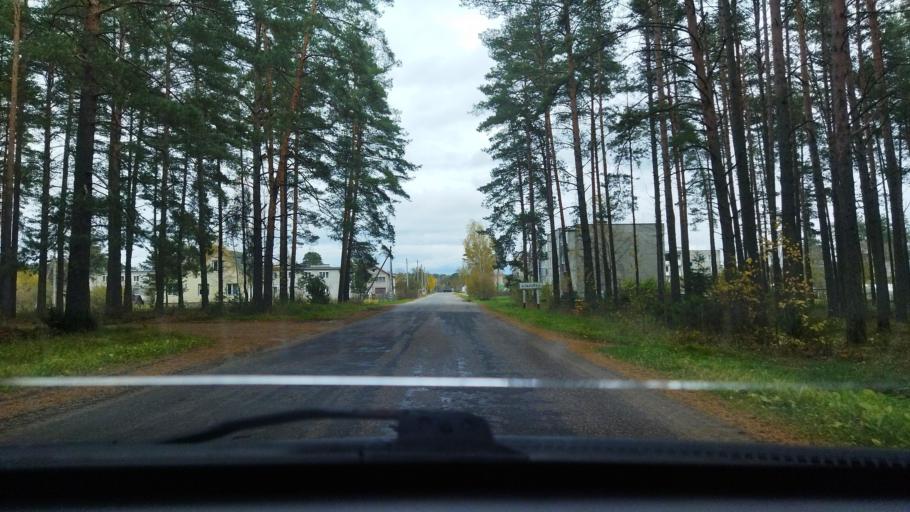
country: BY
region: Minsk
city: Svir
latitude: 54.8088
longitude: 26.2259
